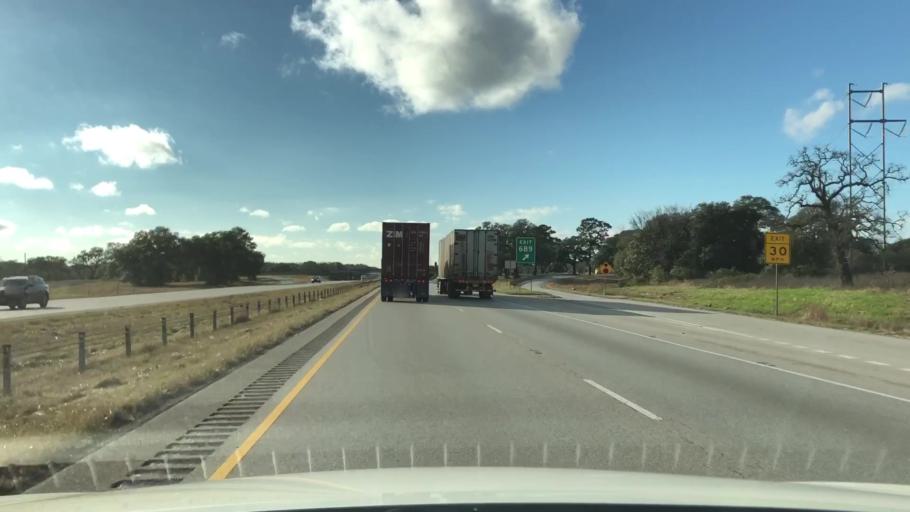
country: US
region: Texas
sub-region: Colorado County
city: Columbus
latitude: 29.6924
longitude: -96.6439
